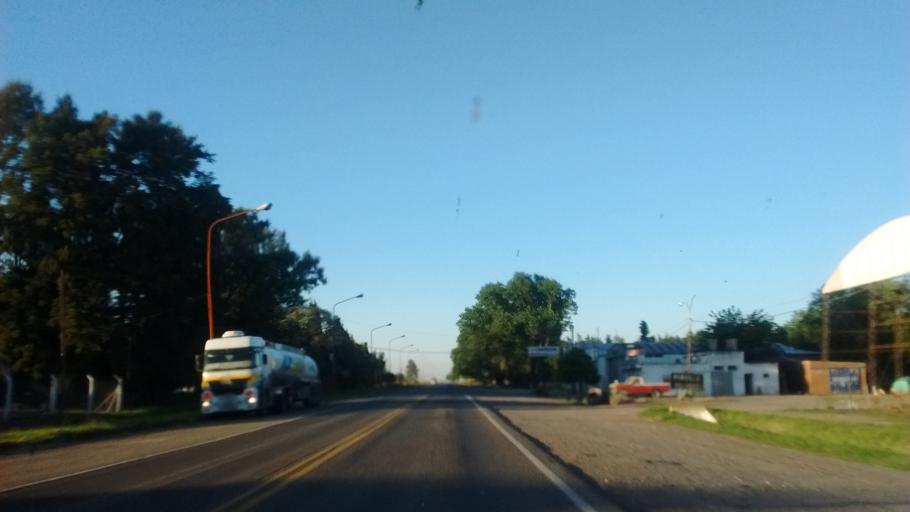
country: AR
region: Santa Fe
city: Firmat
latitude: -33.2521
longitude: -61.3648
